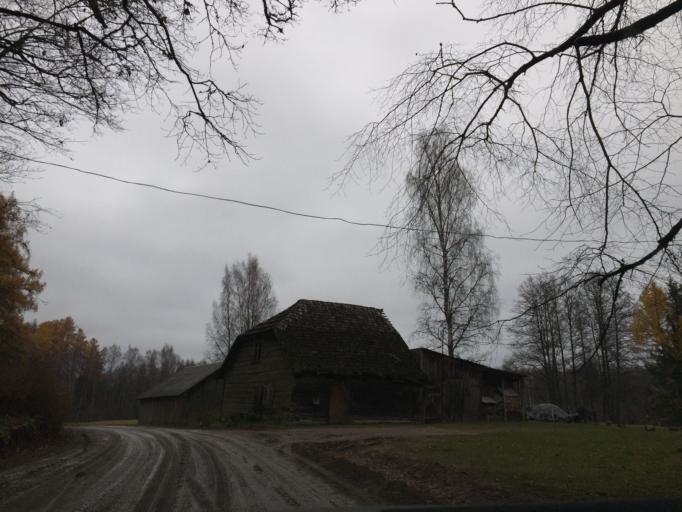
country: LV
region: Pargaujas
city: Stalbe
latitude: 57.5078
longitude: 25.0020
